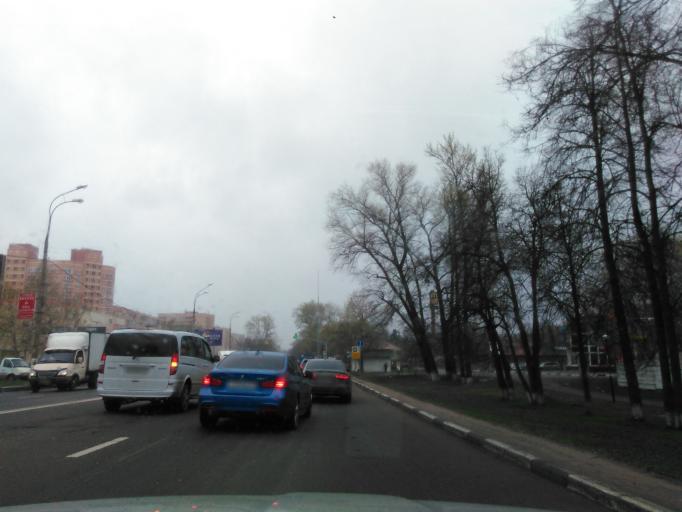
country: RU
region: Moskovskaya
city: Krasnogorsk
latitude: 55.8305
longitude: 37.3051
